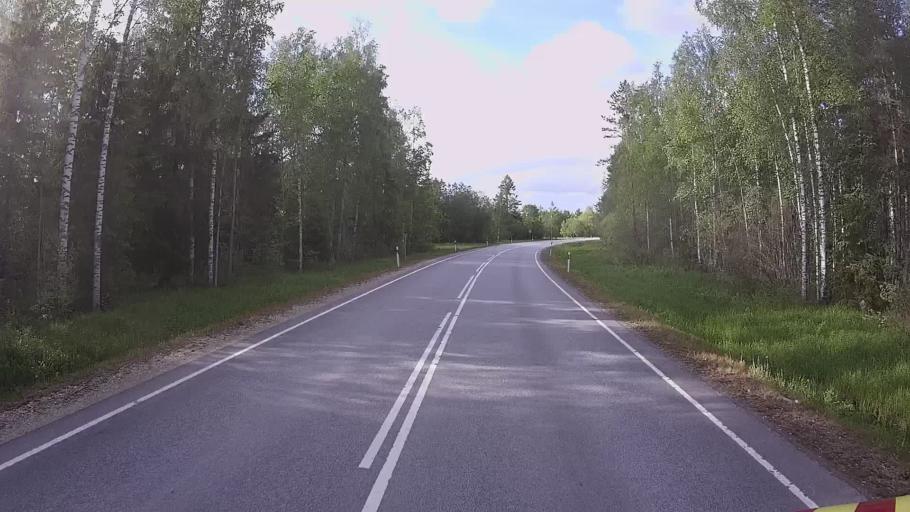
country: EE
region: Jogevamaa
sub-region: Mustvee linn
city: Mustvee
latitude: 58.9740
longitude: 26.8271
